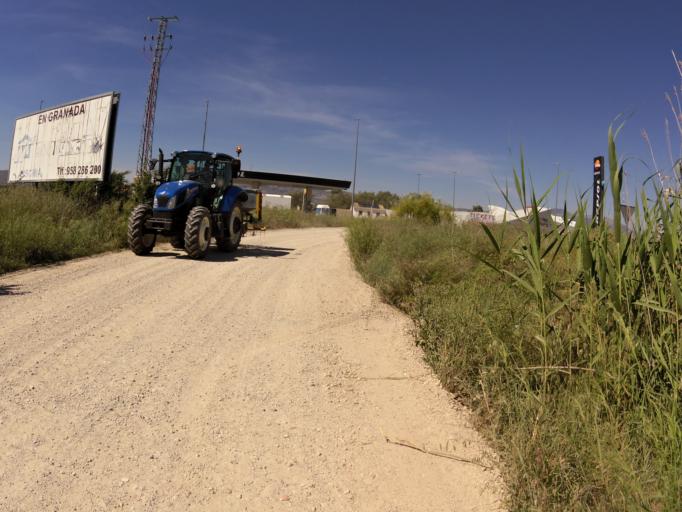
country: ES
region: Andalusia
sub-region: Provincia de Granada
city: Huetor-Tajar
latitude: 37.1811
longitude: -4.0576
